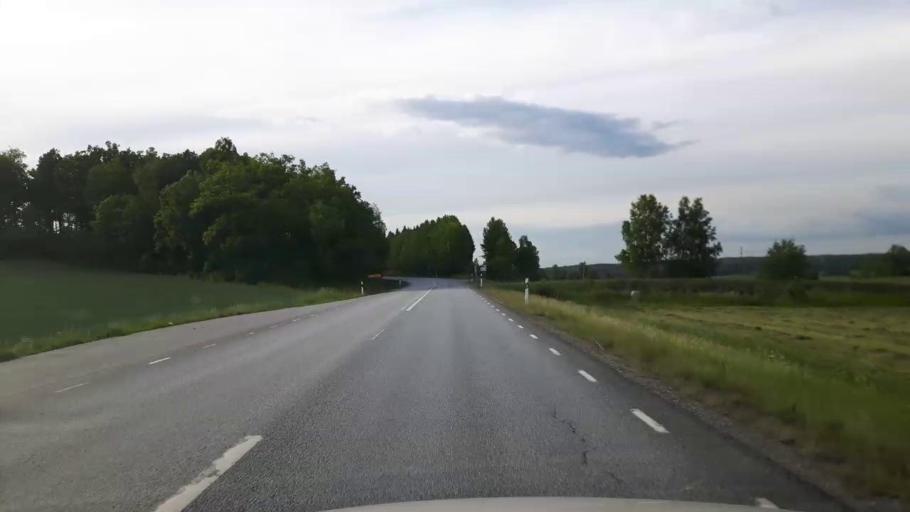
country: SE
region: Uppsala
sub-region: Habo Kommun
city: Balsta
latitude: 59.6489
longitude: 17.5635
